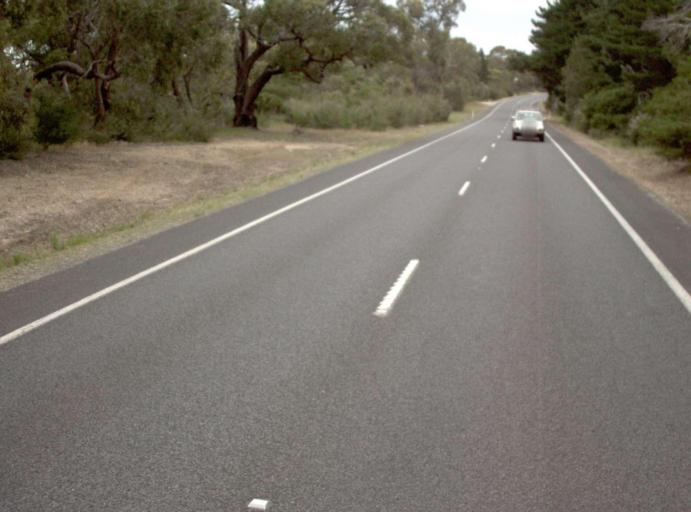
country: AU
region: Victoria
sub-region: Wellington
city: Sale
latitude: -38.1943
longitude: 147.0786
